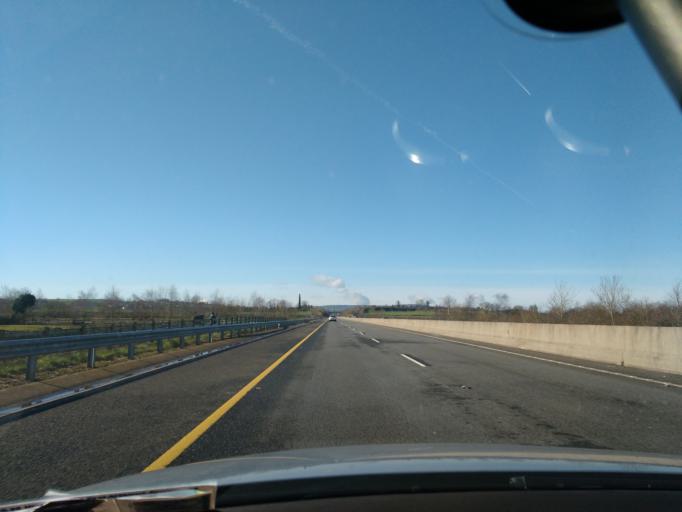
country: IE
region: Munster
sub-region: North Tipperary
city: Nenagh
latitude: 52.8464
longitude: -8.1908
